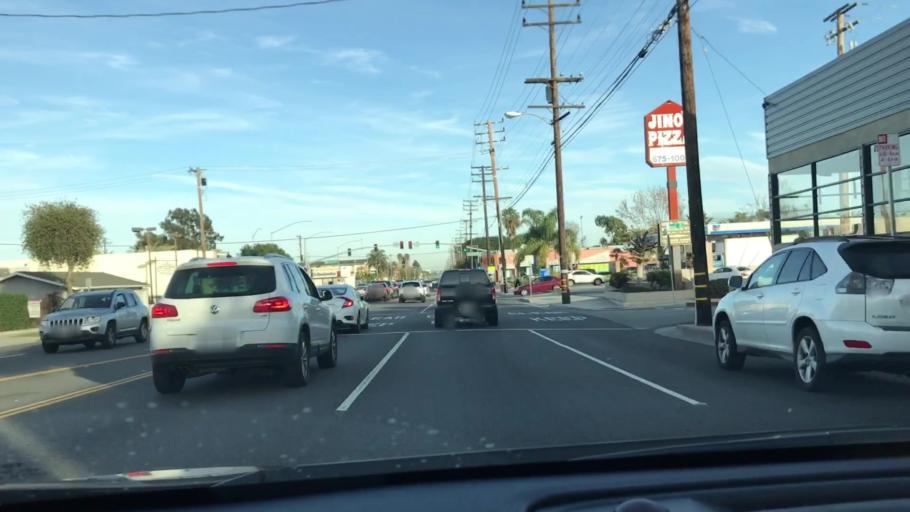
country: US
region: California
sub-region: Los Angeles County
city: Hawthorne
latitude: 33.9018
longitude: -118.3542
